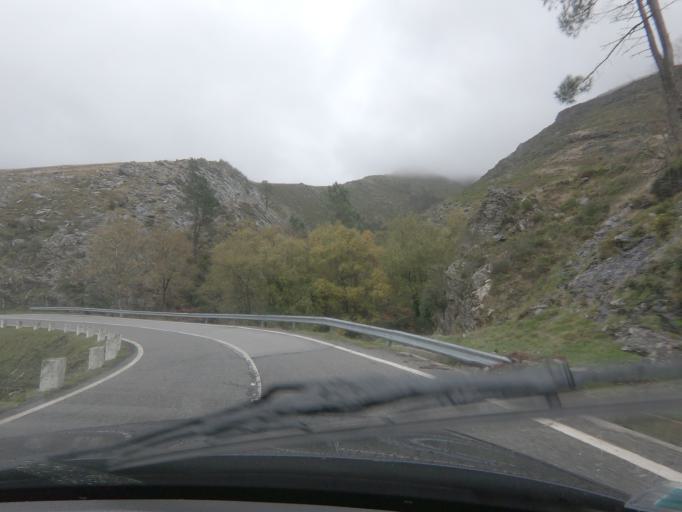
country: PT
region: Vila Real
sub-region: Mondim de Basto
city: Mondim de Basto
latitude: 41.3343
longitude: -7.8691
